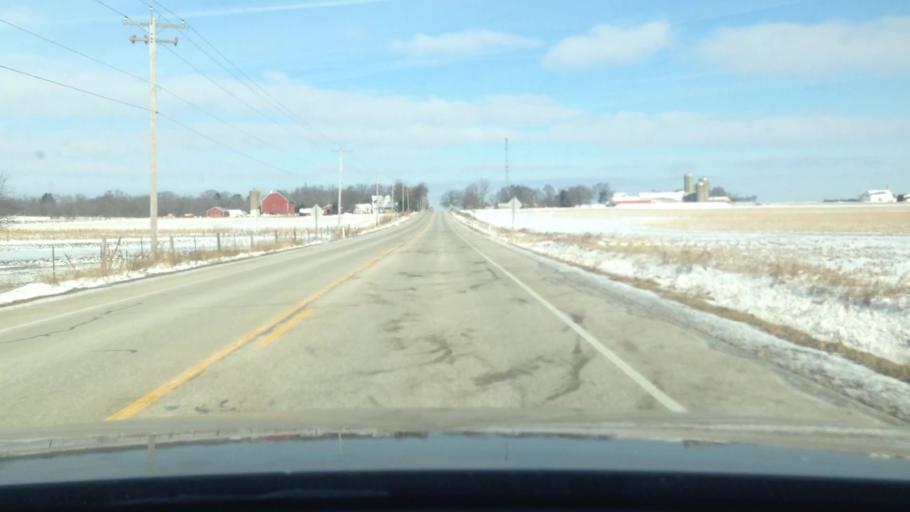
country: US
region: Wisconsin
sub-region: Walworth County
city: Lake Geneva
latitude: 42.6843
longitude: -88.4045
